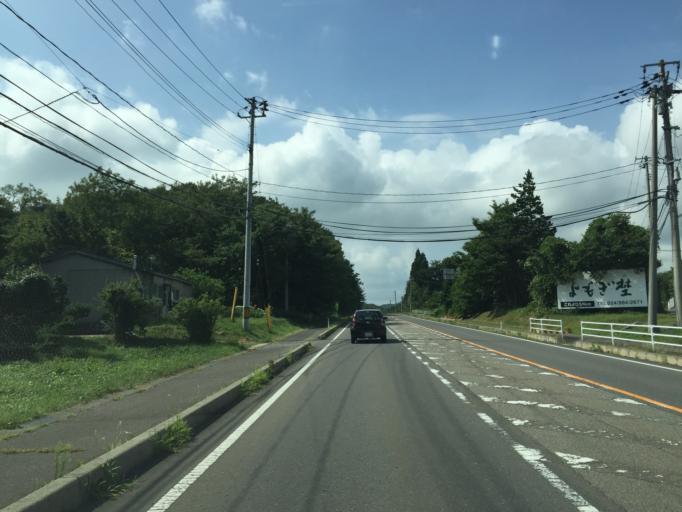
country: JP
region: Fukushima
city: Motomiya
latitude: 37.4955
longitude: 140.2803
